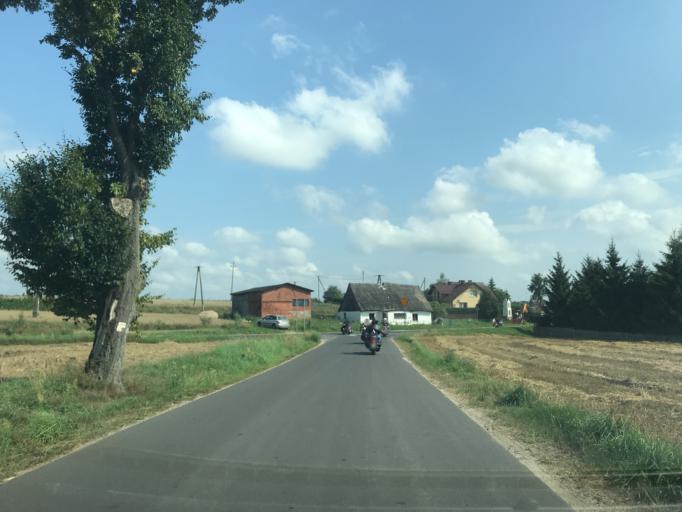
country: PL
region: Warmian-Masurian Voivodeship
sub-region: Powiat nowomiejski
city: Biskupiec
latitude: 53.4642
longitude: 19.4634
